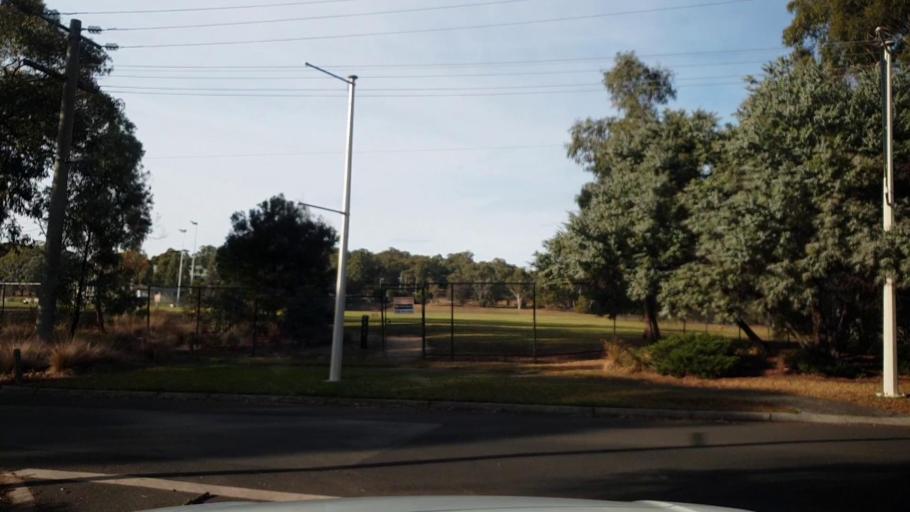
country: AU
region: Victoria
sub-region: Knox
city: Wantirna South
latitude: -37.8919
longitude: 145.1923
